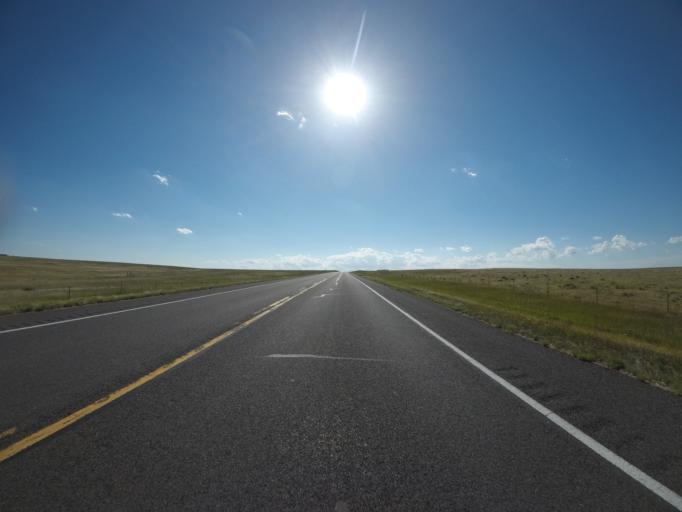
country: US
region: Colorado
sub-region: Logan County
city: Sterling
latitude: 40.6110
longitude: -103.5569
